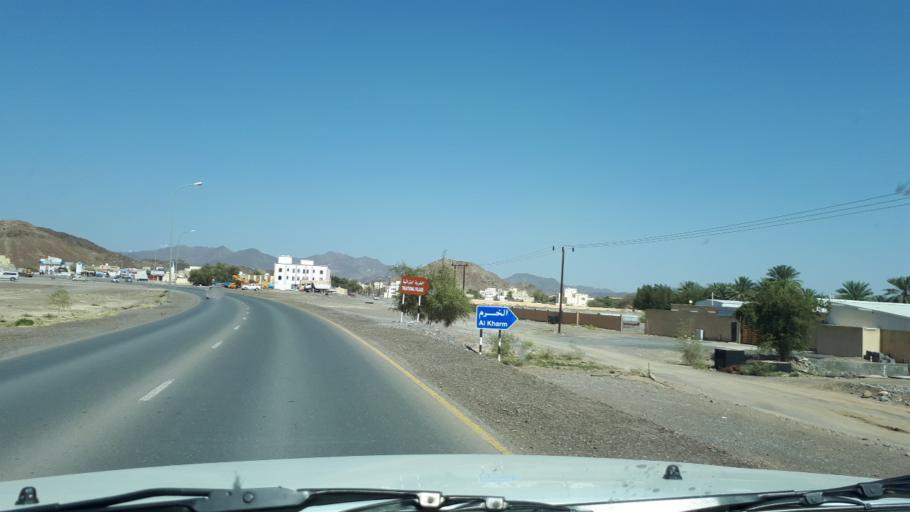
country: OM
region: Muhafazat ad Dakhiliyah
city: Bahla'
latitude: 22.9473
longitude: 57.2810
